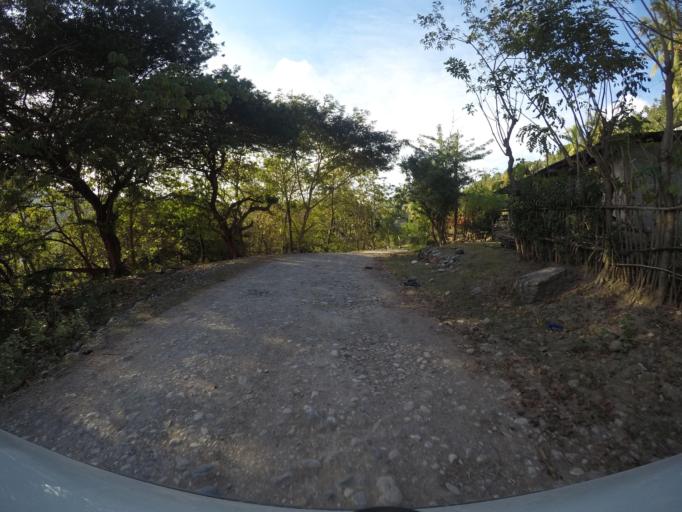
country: TL
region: Viqueque
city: Viqueque
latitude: -8.7987
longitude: 126.5612
